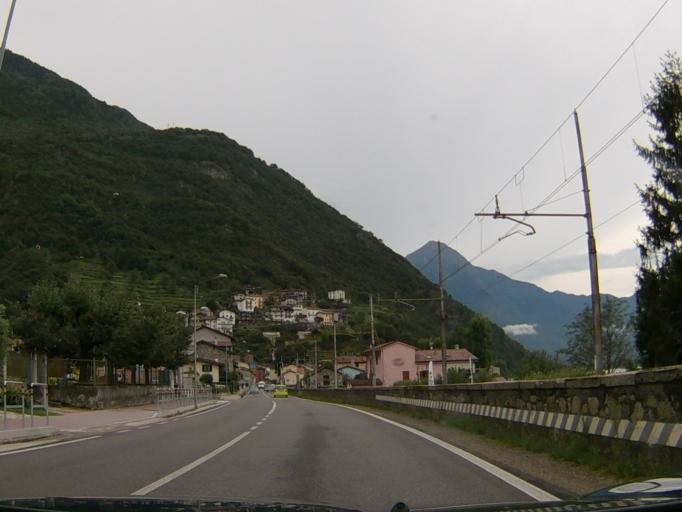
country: IT
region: Lombardy
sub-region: Provincia di Sondrio
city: Verceia
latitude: 46.1985
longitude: 9.4516
